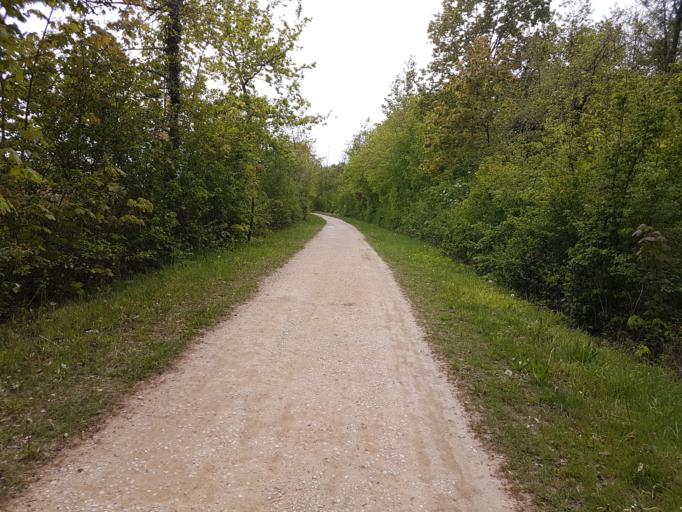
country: CH
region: Aargau
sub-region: Bezirk Brugg
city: Veltheim
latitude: 47.4344
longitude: 8.1606
